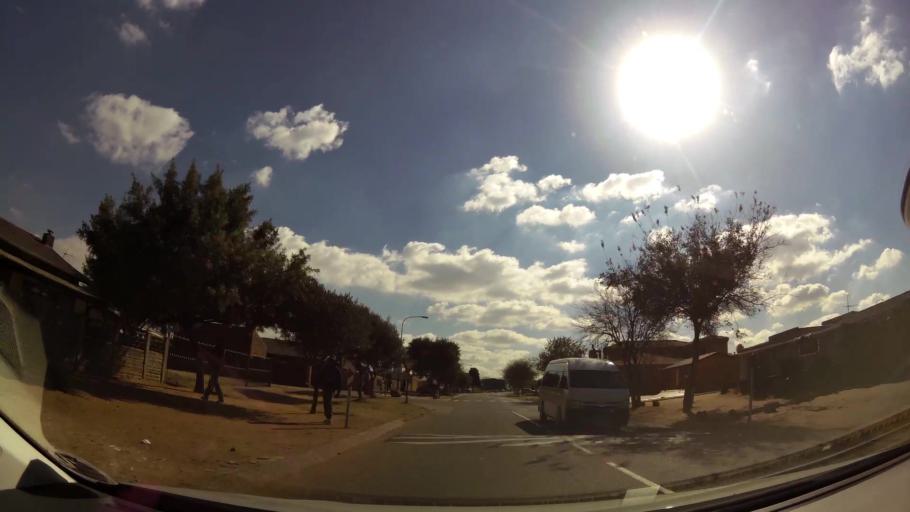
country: ZA
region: Gauteng
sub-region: City of Johannesburg Metropolitan Municipality
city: Roodepoort
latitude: -26.2124
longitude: 27.8801
